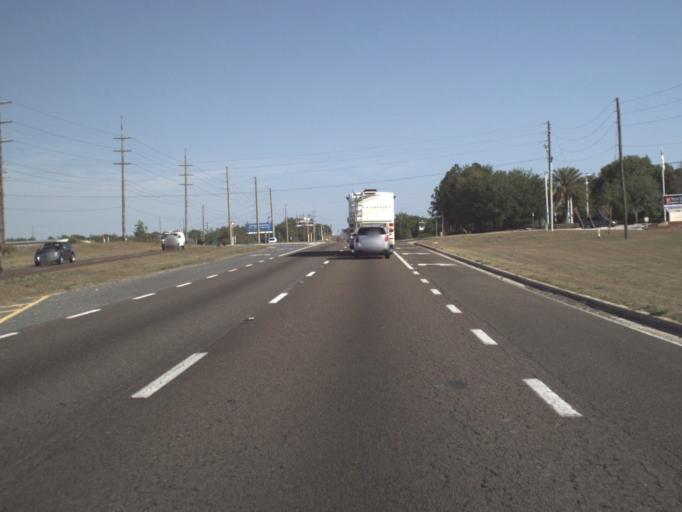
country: US
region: Florida
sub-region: Lake County
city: Minneola
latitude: 28.5948
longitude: -81.7530
